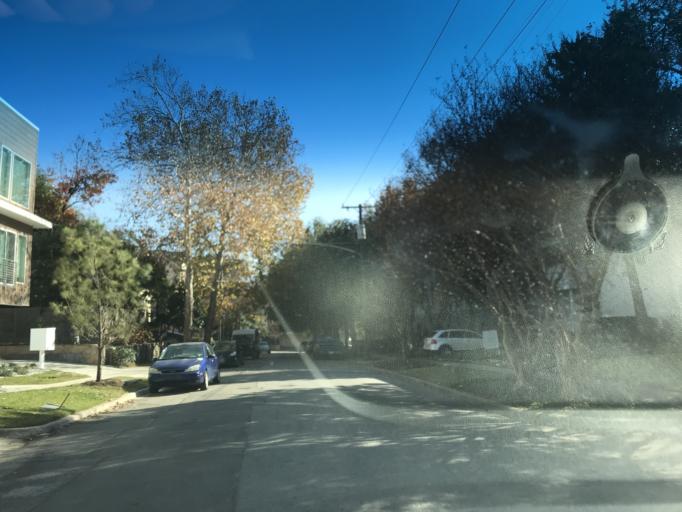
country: US
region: Texas
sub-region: Dallas County
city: Dallas
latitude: 32.8038
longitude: -96.8108
